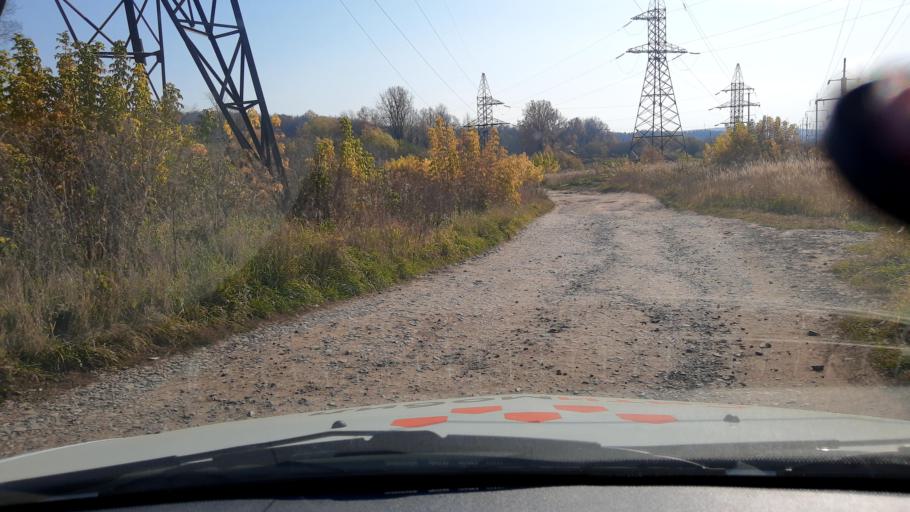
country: RU
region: Bashkortostan
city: Ufa
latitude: 54.8643
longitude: 56.1301
